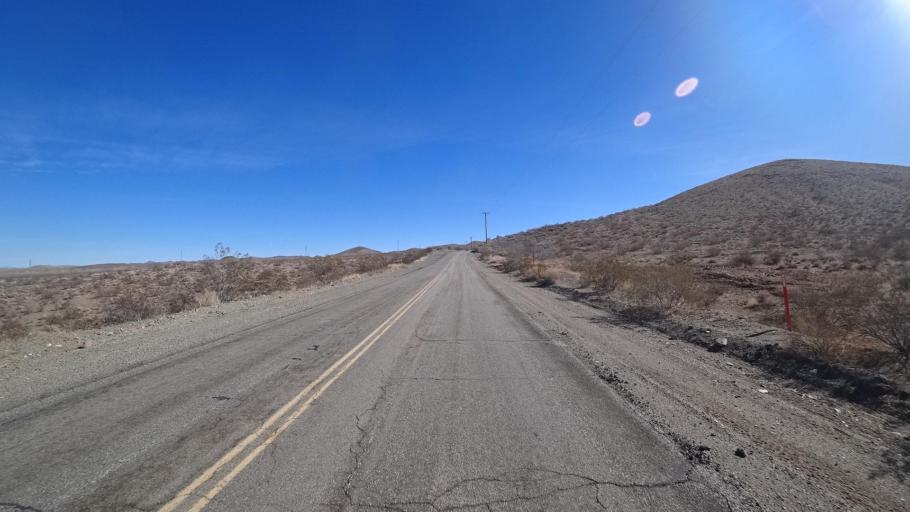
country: US
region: California
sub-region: Kern County
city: Ridgecrest
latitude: 35.3800
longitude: -117.6733
